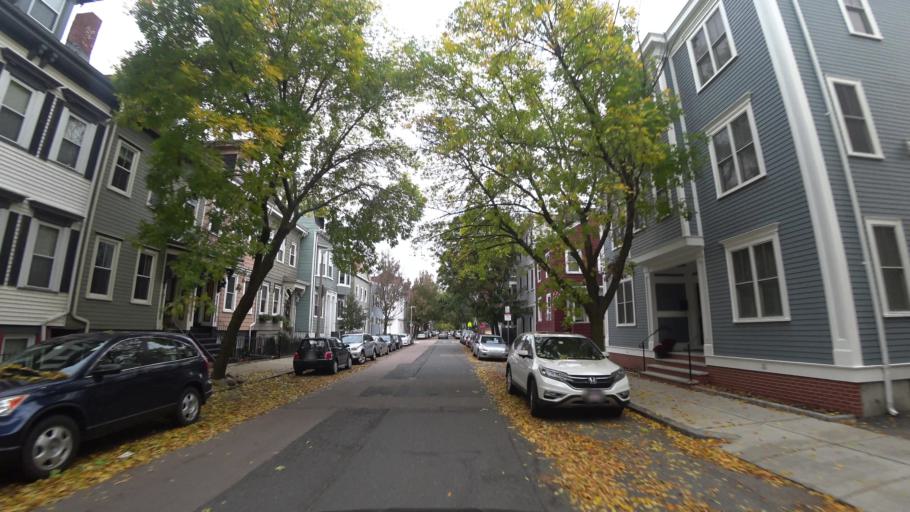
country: US
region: Massachusetts
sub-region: Suffolk County
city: South Boston
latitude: 42.3356
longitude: -71.0478
